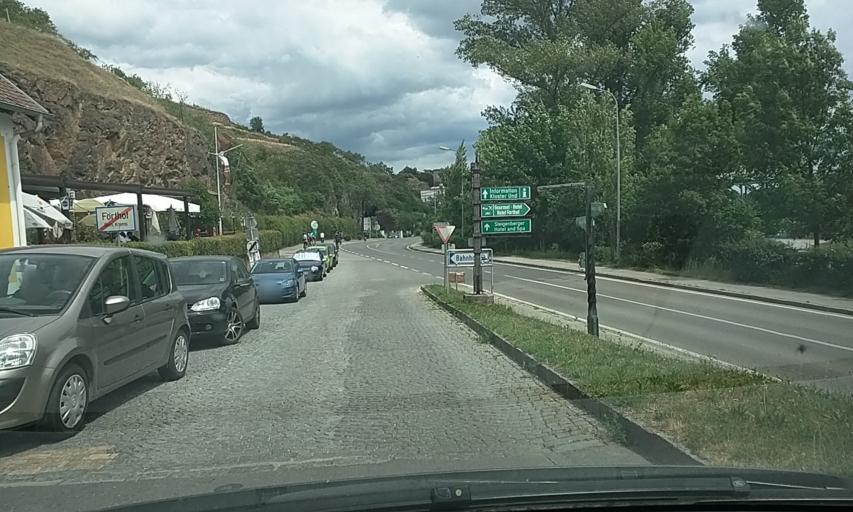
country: AT
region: Lower Austria
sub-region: Politischer Bezirk Krems
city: Weinzierl bei Krems
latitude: 48.3992
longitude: 15.5721
